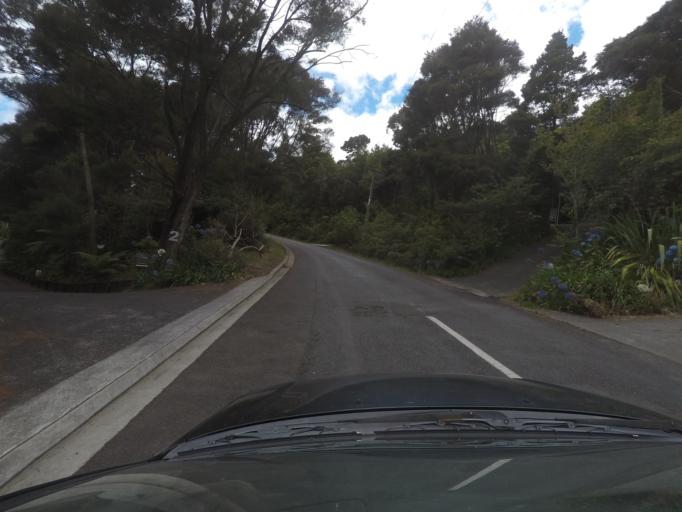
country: NZ
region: Northland
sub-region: Far North District
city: Paihia
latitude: -35.2900
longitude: 174.0969
